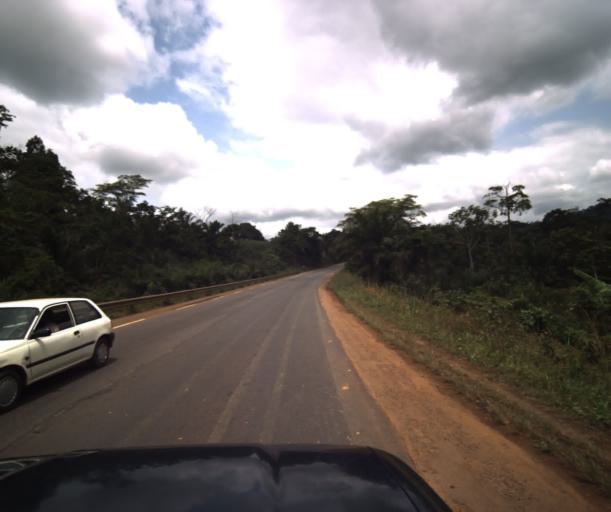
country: CM
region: Centre
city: Mbankomo
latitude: 3.7771
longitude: 11.0768
